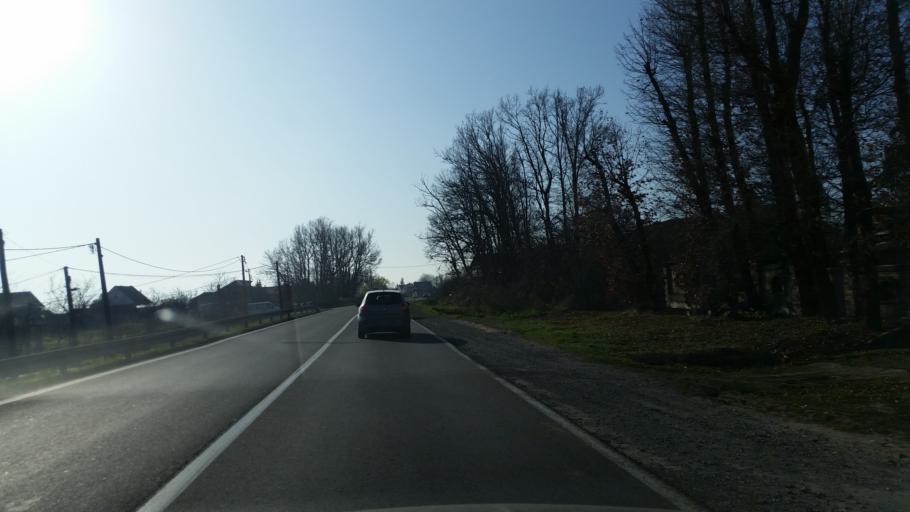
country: RS
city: Vranic
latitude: 44.6027
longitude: 20.3531
